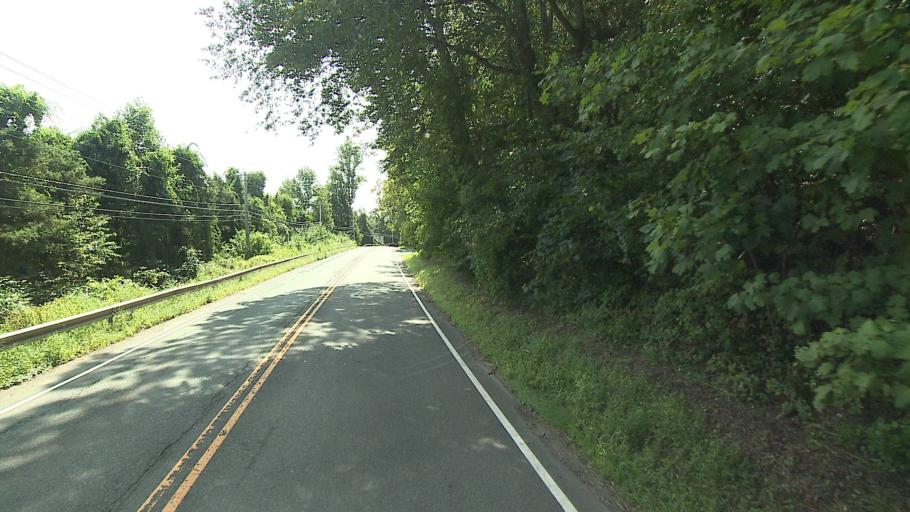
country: US
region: Connecticut
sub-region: Fairfield County
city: Trumbull
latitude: 41.2540
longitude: -73.2818
